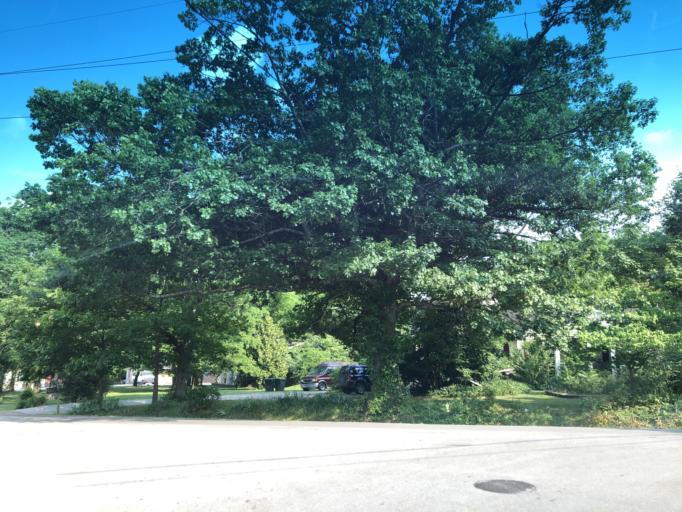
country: US
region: Tennessee
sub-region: Davidson County
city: Goodlettsville
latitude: 36.2761
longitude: -86.7147
